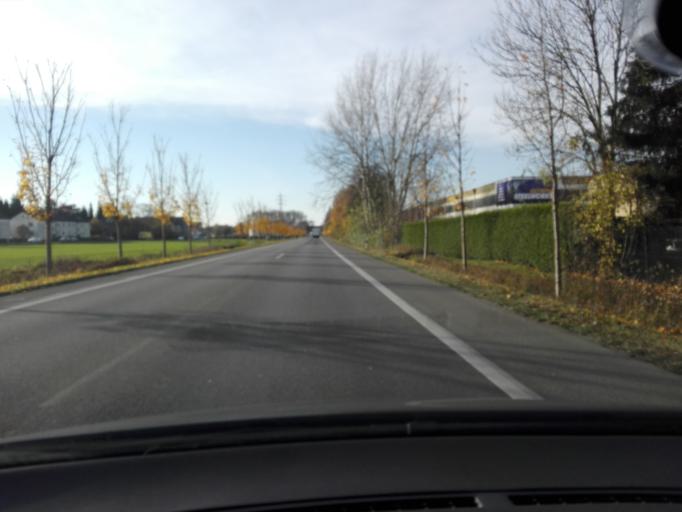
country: DE
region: North Rhine-Westphalia
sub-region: Regierungsbezirk Arnsberg
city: Dortmund
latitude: 51.5276
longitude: 7.5260
